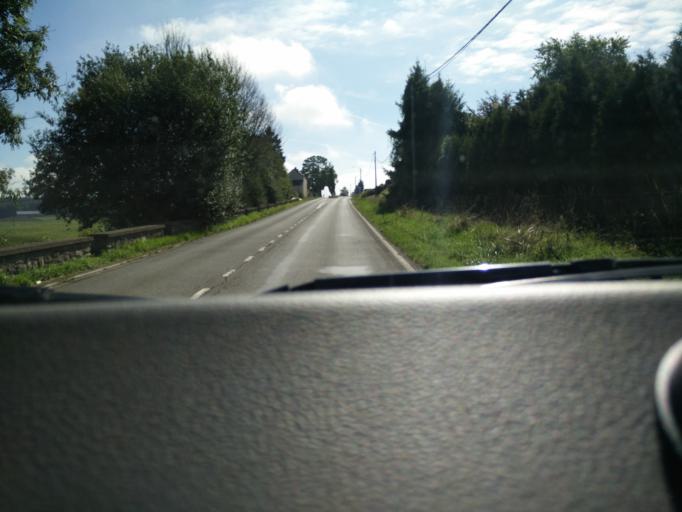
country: BE
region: Wallonia
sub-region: Province de Namur
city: Dinant
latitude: 50.2616
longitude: 4.9663
